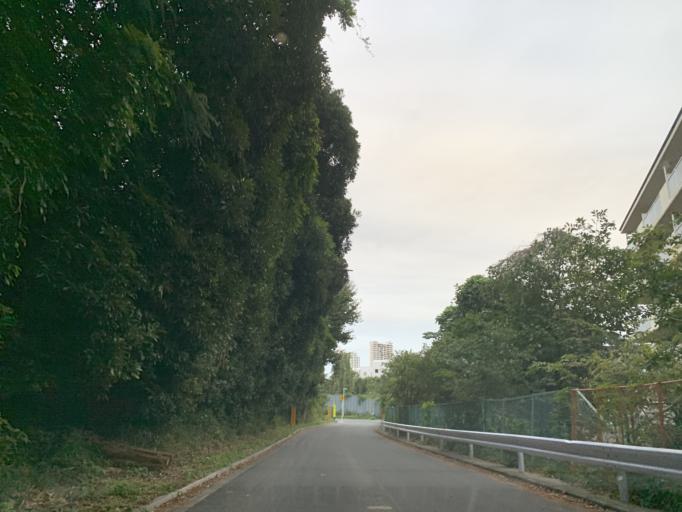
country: JP
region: Chiba
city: Kashiwa
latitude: 35.8984
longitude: 139.9452
